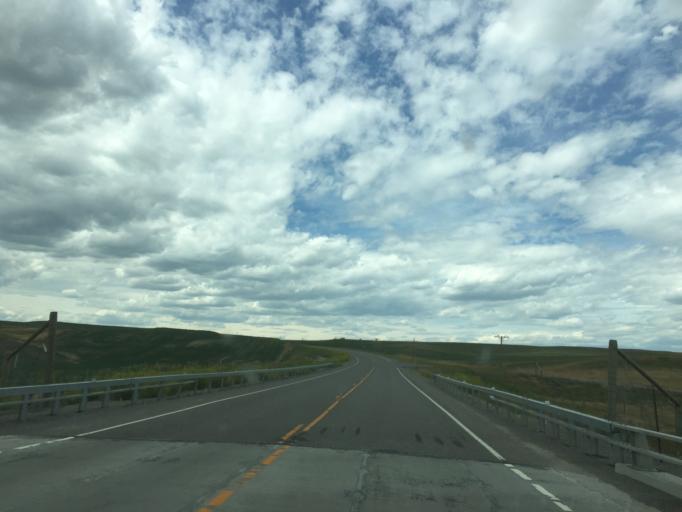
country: US
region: Montana
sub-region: Teton County
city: Choteau
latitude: 48.1349
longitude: -112.3903
